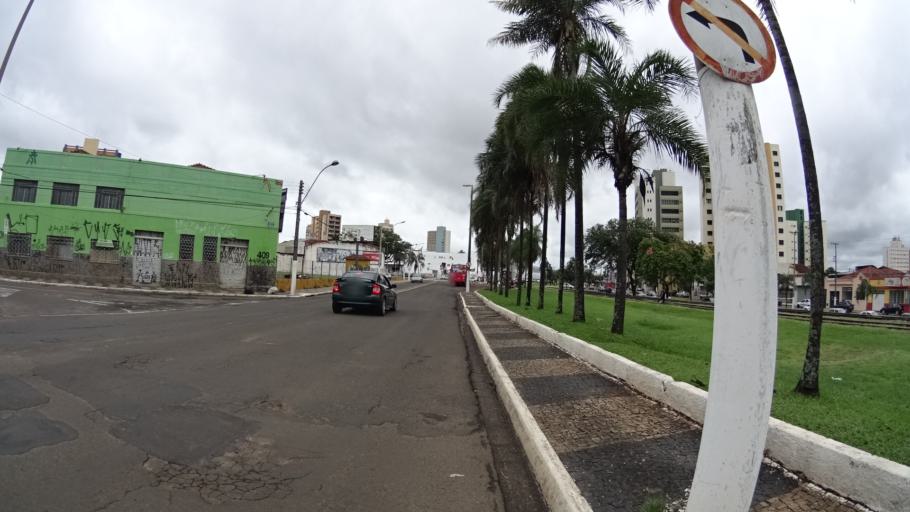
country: BR
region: Sao Paulo
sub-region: Marilia
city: Marilia
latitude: -22.2185
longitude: -49.9448
